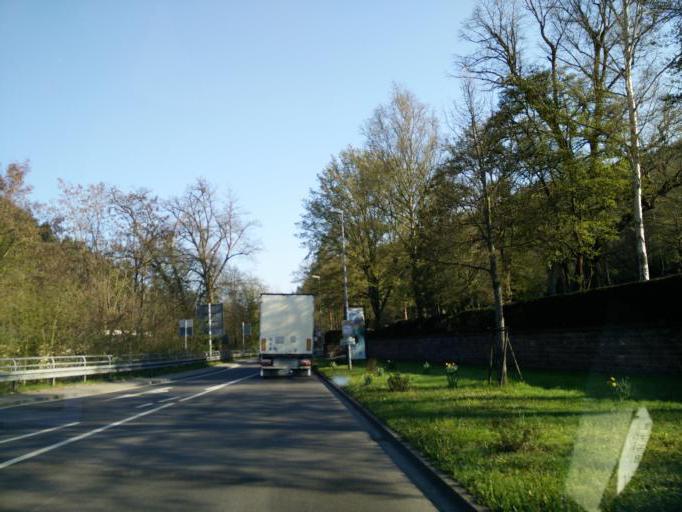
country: DE
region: Baden-Wuerttemberg
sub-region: Karlsruhe Region
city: Calw
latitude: 48.7191
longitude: 8.7378
